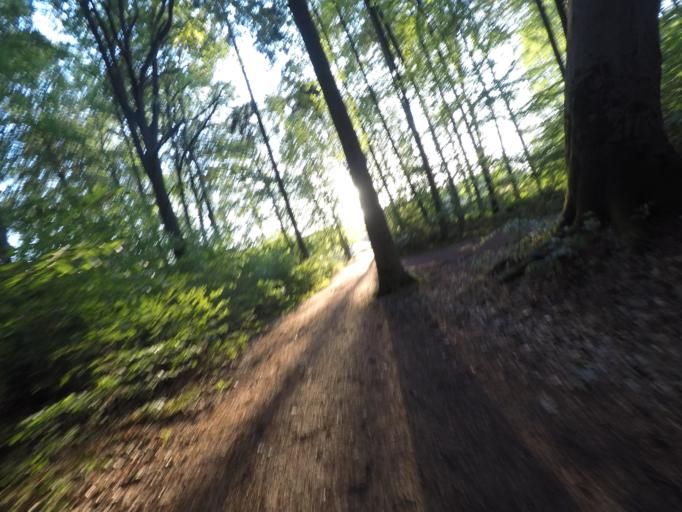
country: DE
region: Brandenburg
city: Marienwerder
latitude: 52.9023
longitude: 13.6647
